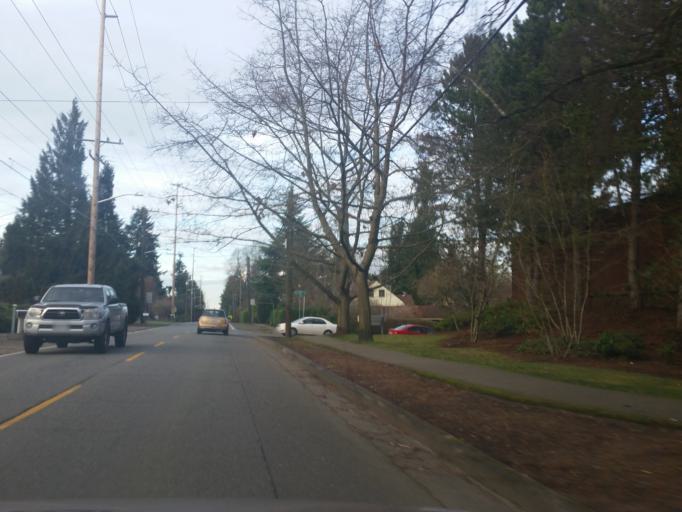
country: US
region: Washington
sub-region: King County
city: Shoreline
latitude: 47.7278
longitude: -122.3290
